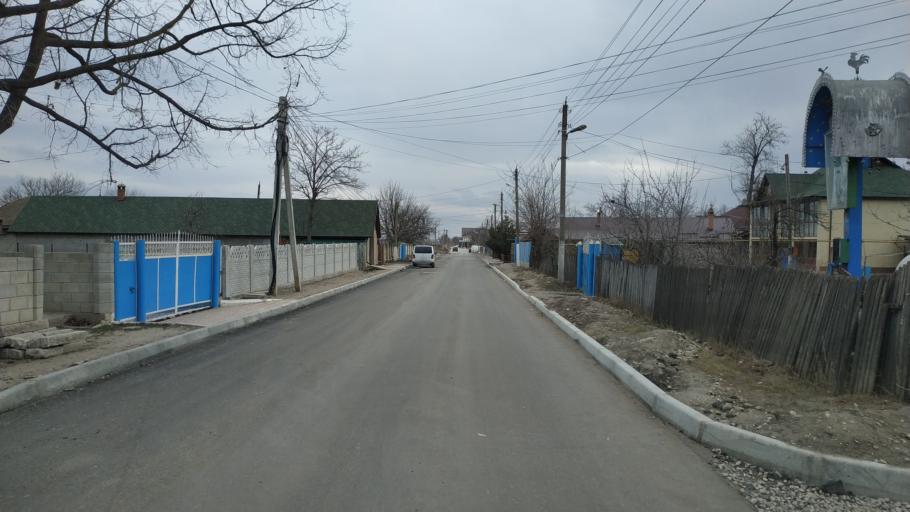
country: MD
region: Laloveni
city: Ialoveni
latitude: 46.8604
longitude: 28.7845
